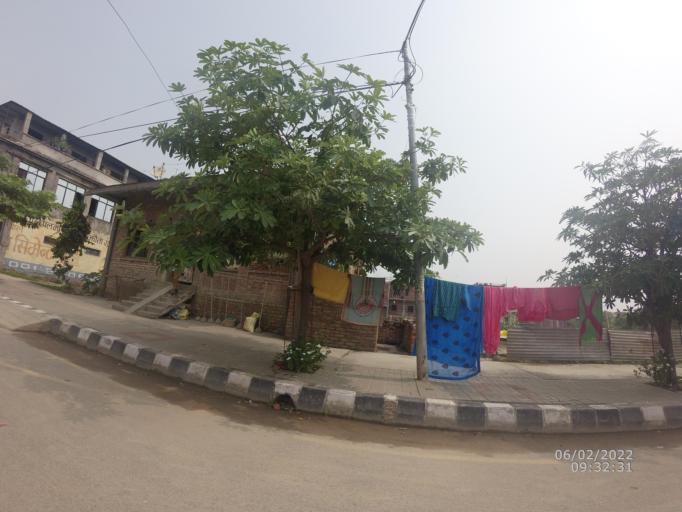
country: NP
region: Western Region
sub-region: Lumbini Zone
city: Bhairahawa
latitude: 27.4983
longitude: 83.4515
